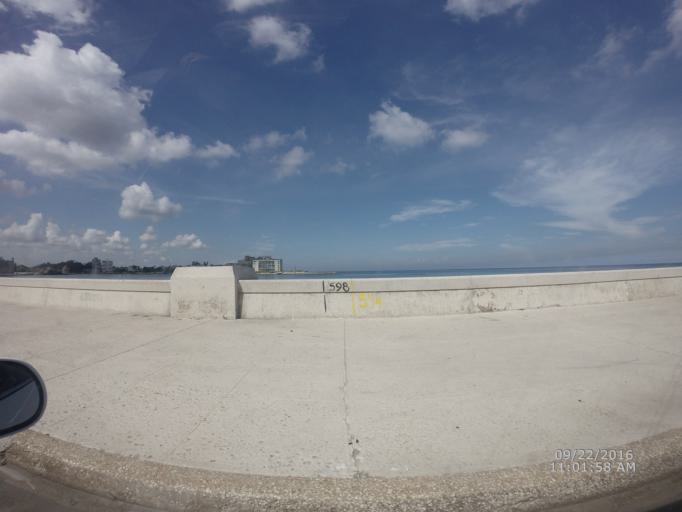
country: CU
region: La Habana
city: Havana
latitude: 23.1349
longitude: -82.4081
